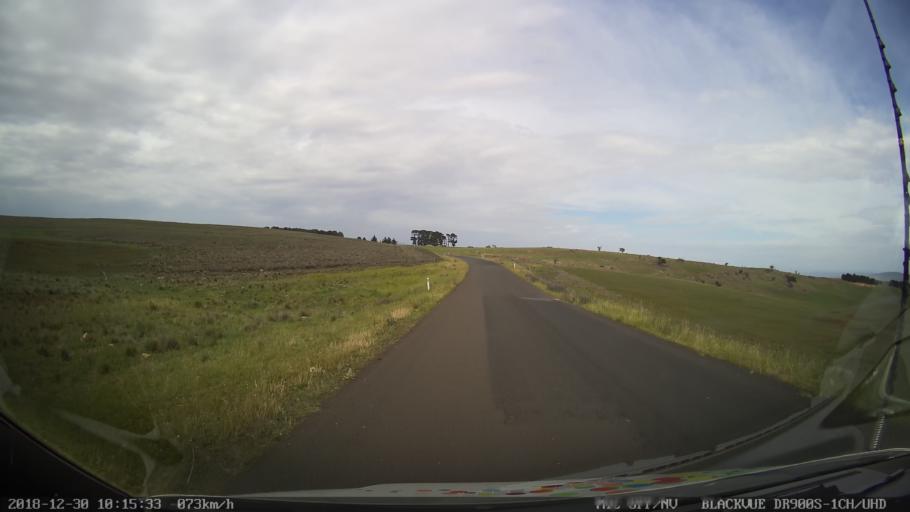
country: AU
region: New South Wales
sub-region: Snowy River
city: Berridale
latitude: -36.5433
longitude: 149.0447
